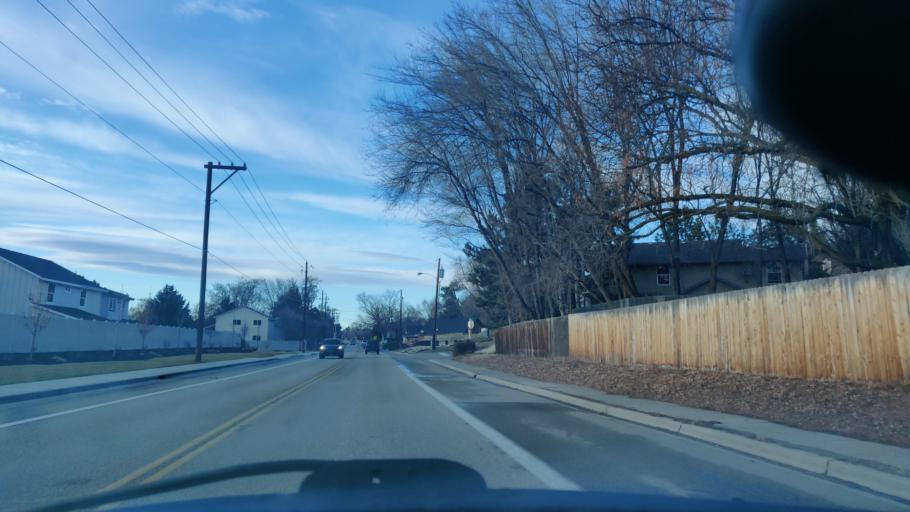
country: US
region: Idaho
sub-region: Ada County
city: Garden City
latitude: 43.6527
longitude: -116.2292
